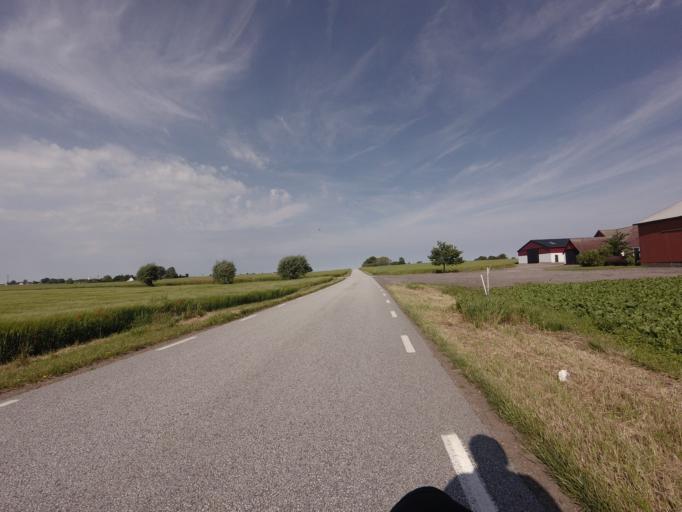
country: SE
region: Skane
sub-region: Malmo
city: Oxie
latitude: 55.4956
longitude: 13.0703
